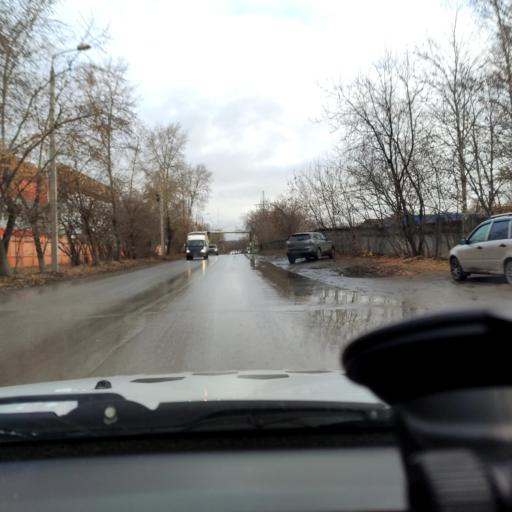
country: RU
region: Perm
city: Perm
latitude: 57.9785
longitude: 56.2692
